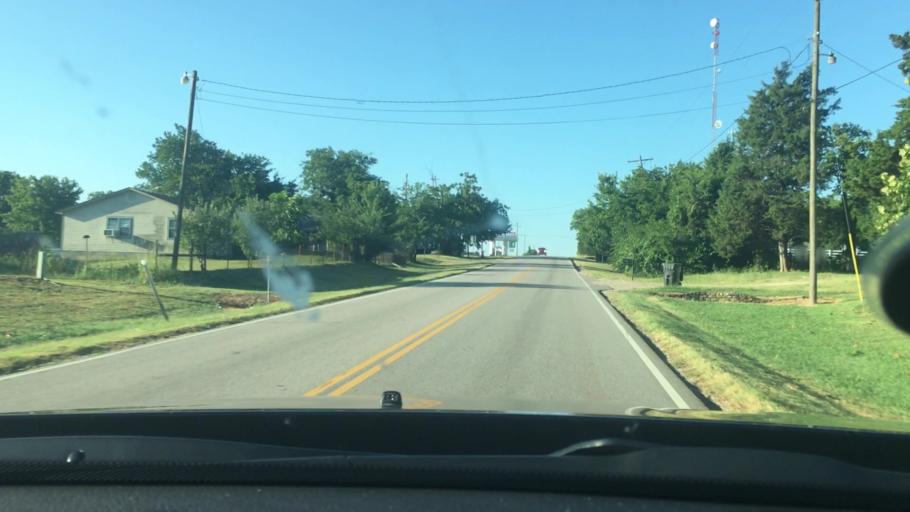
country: US
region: Oklahoma
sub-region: Murray County
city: Sulphur
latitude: 34.6229
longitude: -96.8447
